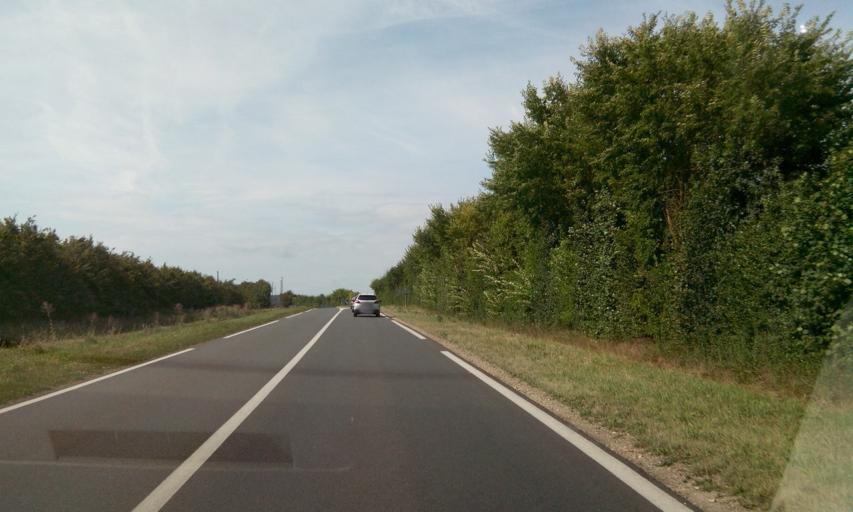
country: FR
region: Poitou-Charentes
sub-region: Departement de la Vienne
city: Civray
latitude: 46.1543
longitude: 0.2810
